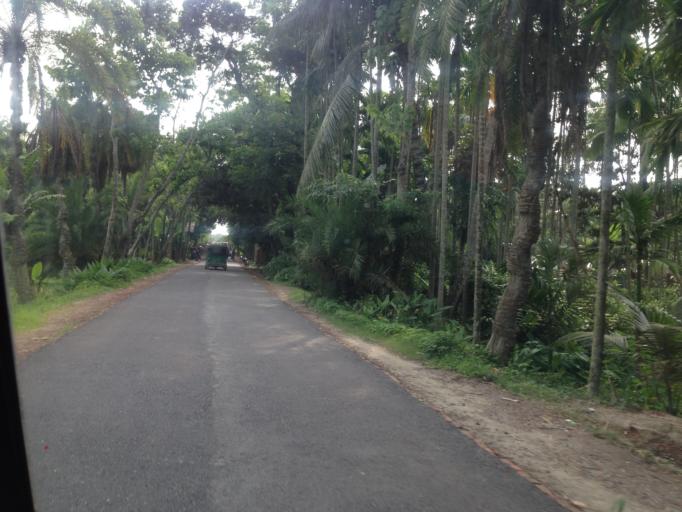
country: BD
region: Chittagong
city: Raipur
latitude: 23.0346
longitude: 90.7181
